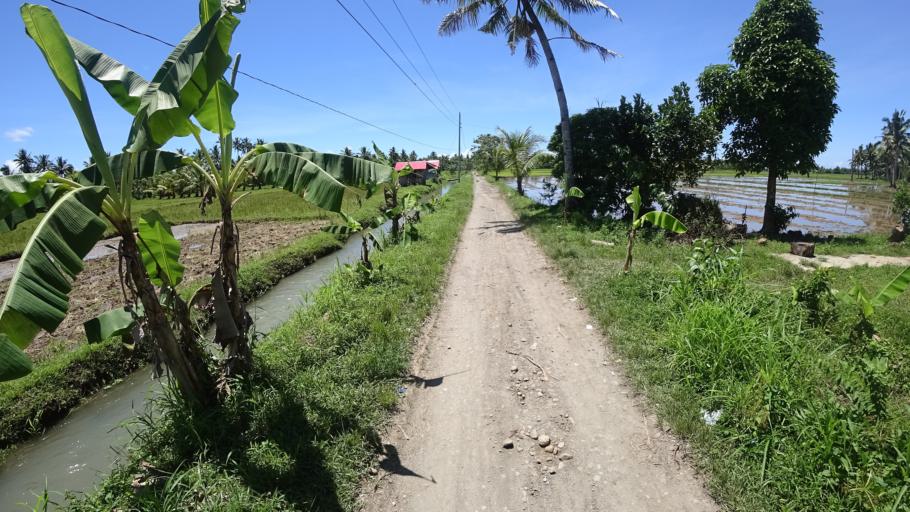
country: PH
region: Eastern Visayas
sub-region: Province of Leyte
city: MacArthur
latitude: 10.8518
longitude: 124.9673
